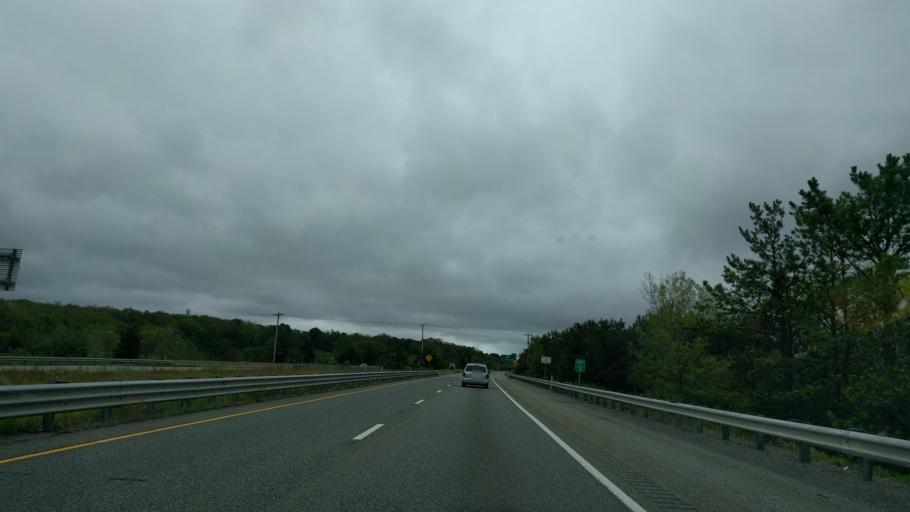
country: US
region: Massachusetts
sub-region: Worcester County
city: Millville
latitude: 42.0244
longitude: -71.6054
